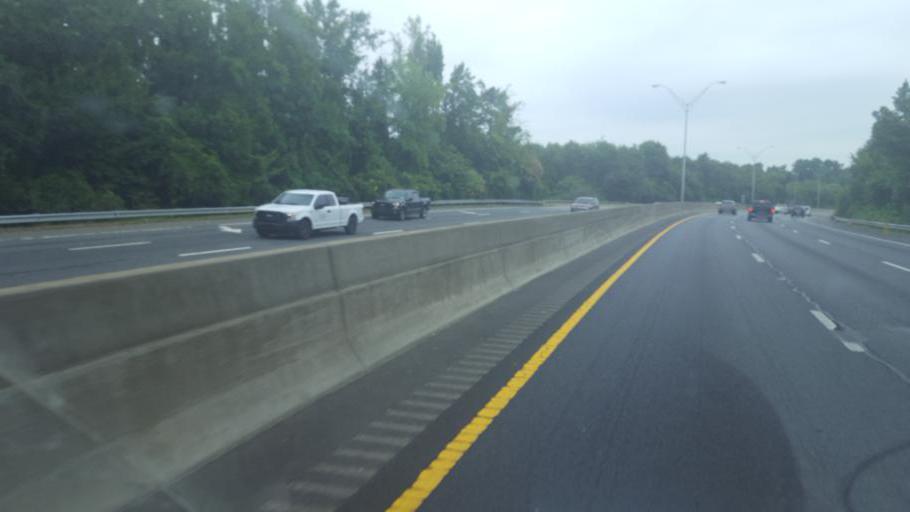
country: US
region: North Carolina
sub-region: Mecklenburg County
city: Charlotte
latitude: 35.2167
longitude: -80.8721
